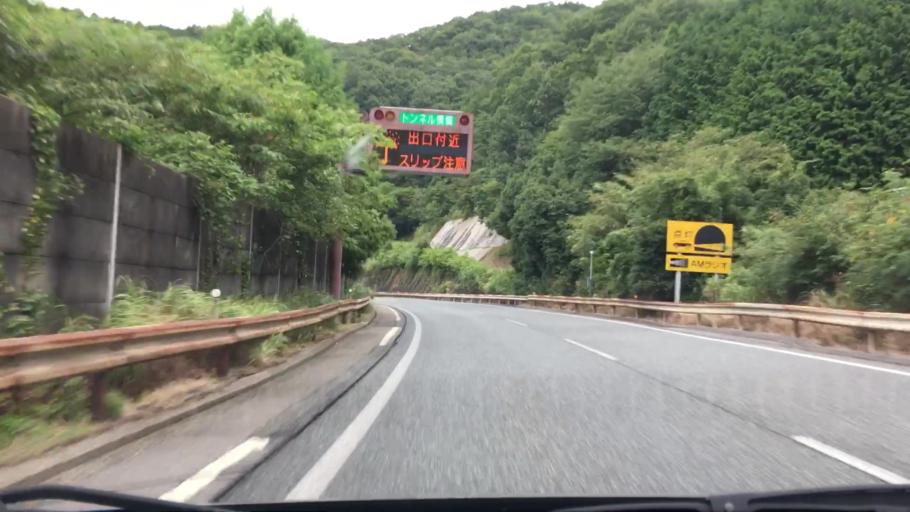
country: JP
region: Okayama
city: Niimi
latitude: 34.9925
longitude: 133.4588
